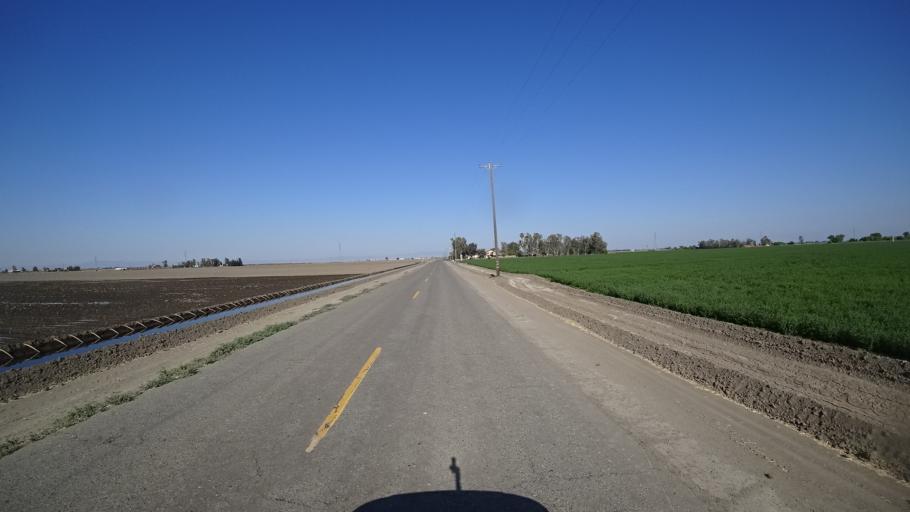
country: US
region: California
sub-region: Kings County
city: Lemoore Station
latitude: 36.3285
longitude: -119.8802
